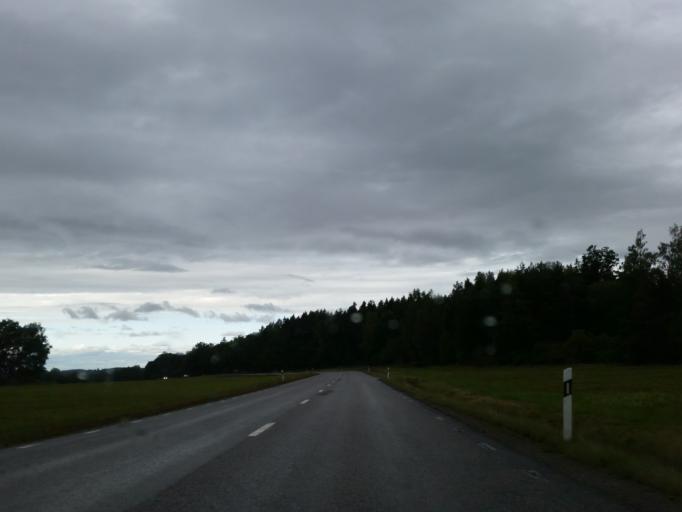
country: SE
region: Uppsala
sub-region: Habo Kommun
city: Balsta
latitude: 59.6484
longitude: 17.4253
